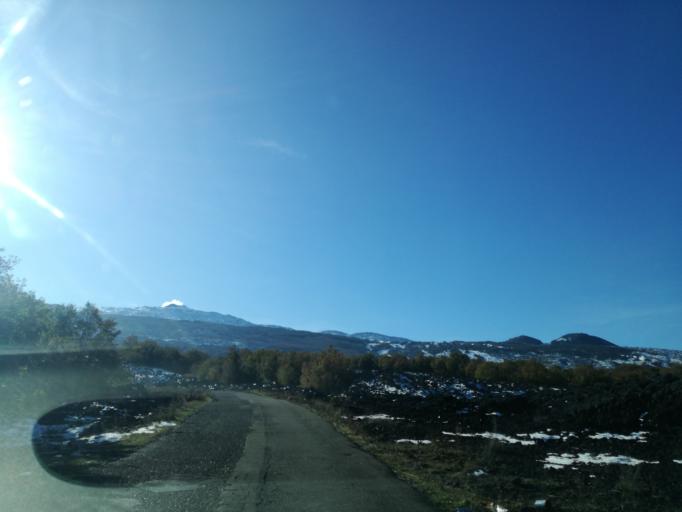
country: IT
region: Sicily
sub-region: Catania
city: Randazzo
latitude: 37.8604
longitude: 14.9802
